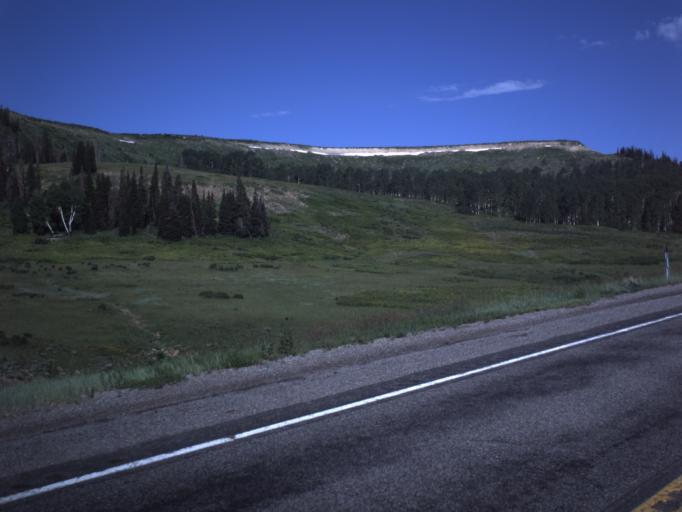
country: US
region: Utah
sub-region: Sanpete County
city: Fairview
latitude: 39.6072
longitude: -111.2787
